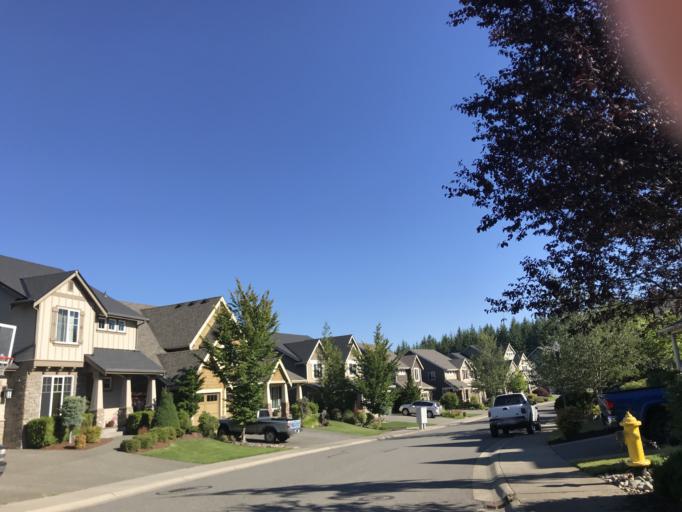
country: US
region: Washington
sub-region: King County
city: Ravensdale
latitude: 47.3547
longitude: -122.0046
